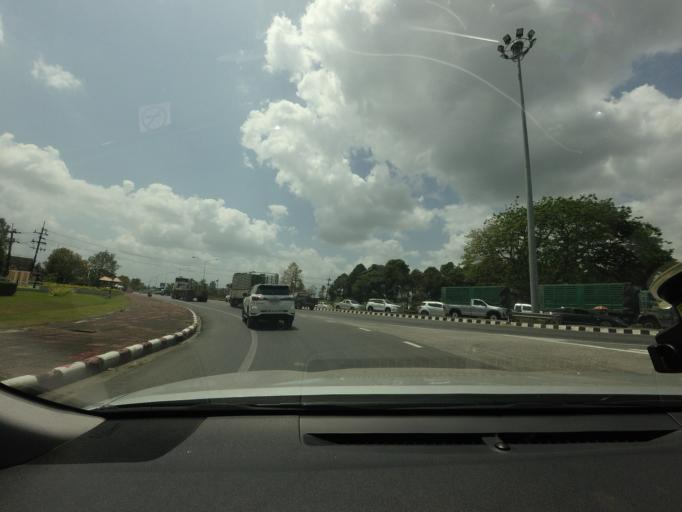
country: TH
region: Nakhon Si Thammarat
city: Nakhon Si Thammarat
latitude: 8.4337
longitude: 99.9219
